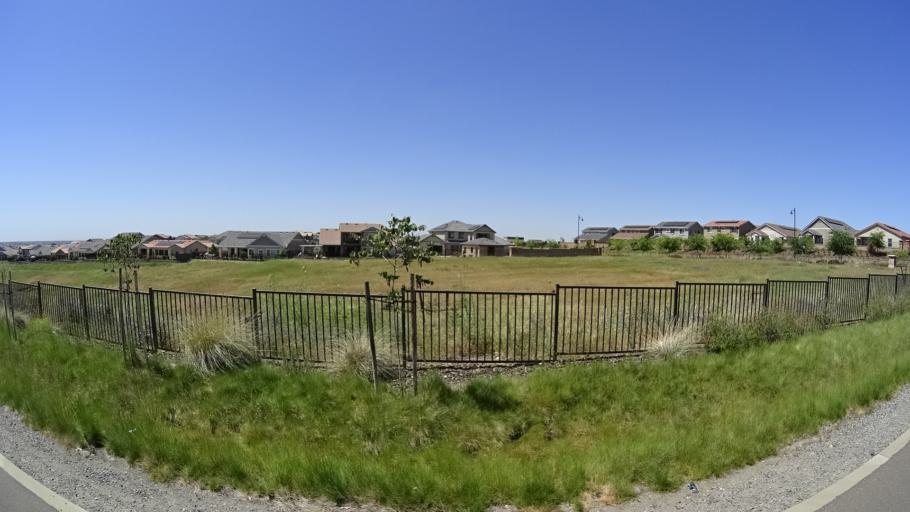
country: US
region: California
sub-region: Placer County
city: Rocklin
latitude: 38.8287
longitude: -121.2659
